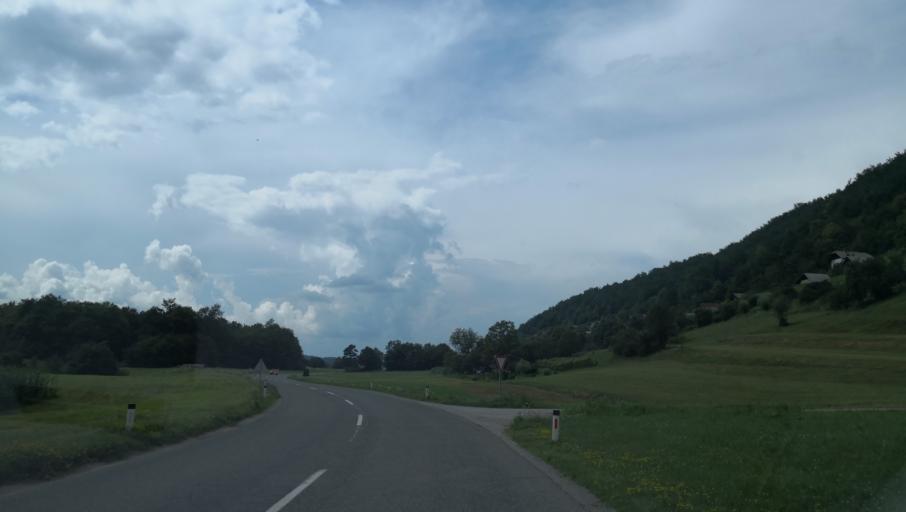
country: SI
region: Zuzemberk
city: Zuzemberk
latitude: 45.7970
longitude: 14.9826
